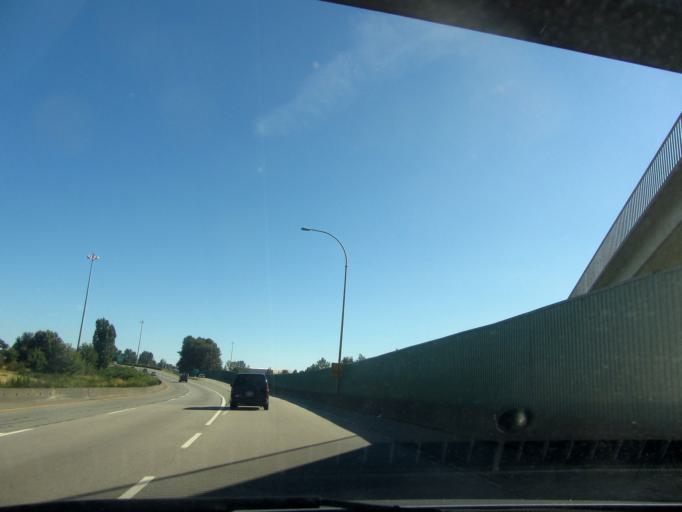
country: CA
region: British Columbia
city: New Westminster
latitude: 49.1797
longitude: -122.9624
